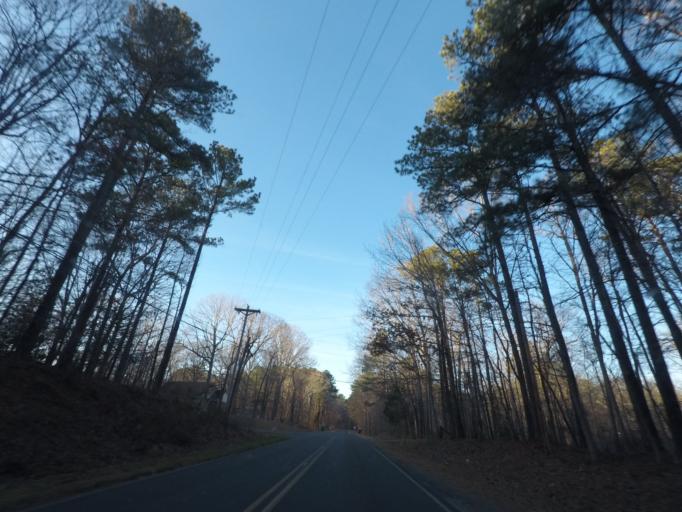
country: US
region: North Carolina
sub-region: Durham County
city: Durham
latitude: 36.0772
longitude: -78.9741
